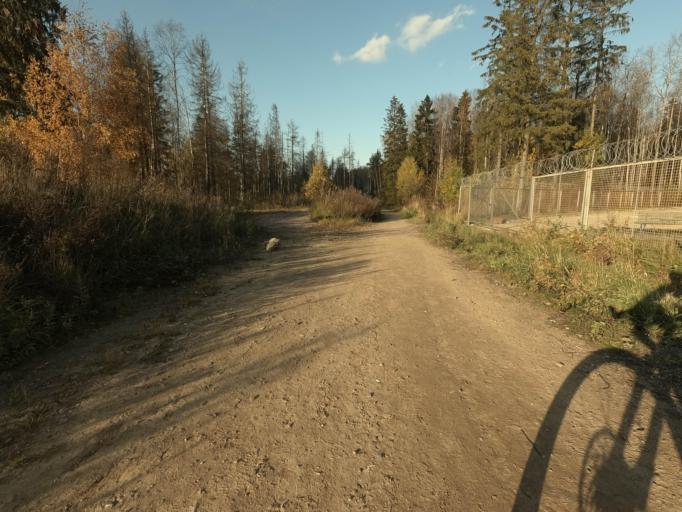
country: RU
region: Leningrad
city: Sertolovo
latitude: 60.1476
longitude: 30.2221
